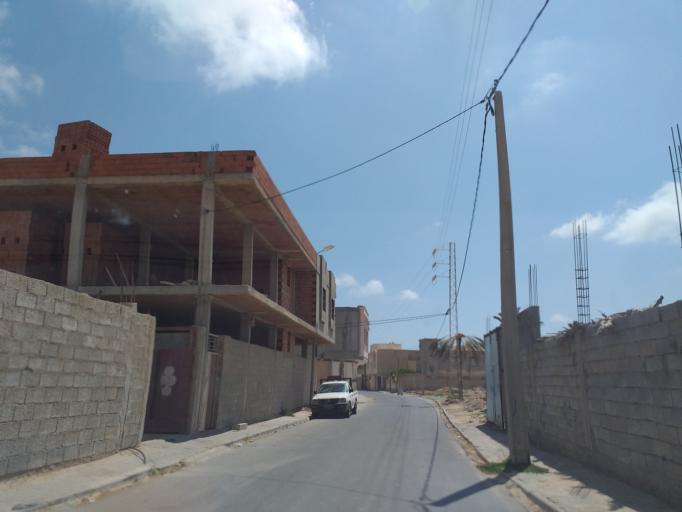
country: TN
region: Qabis
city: Gabes
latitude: 33.9458
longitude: 10.0592
